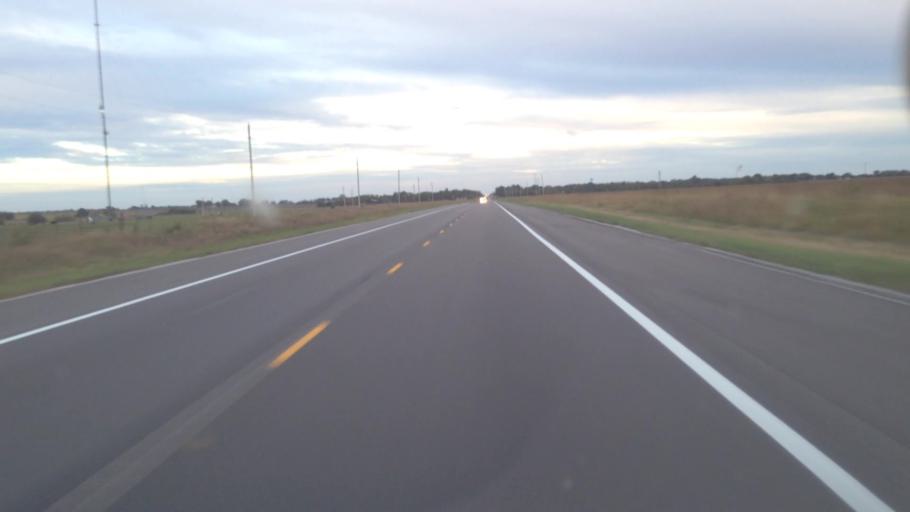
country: US
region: Kansas
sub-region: Anderson County
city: Garnett
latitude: 38.4235
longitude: -95.2487
